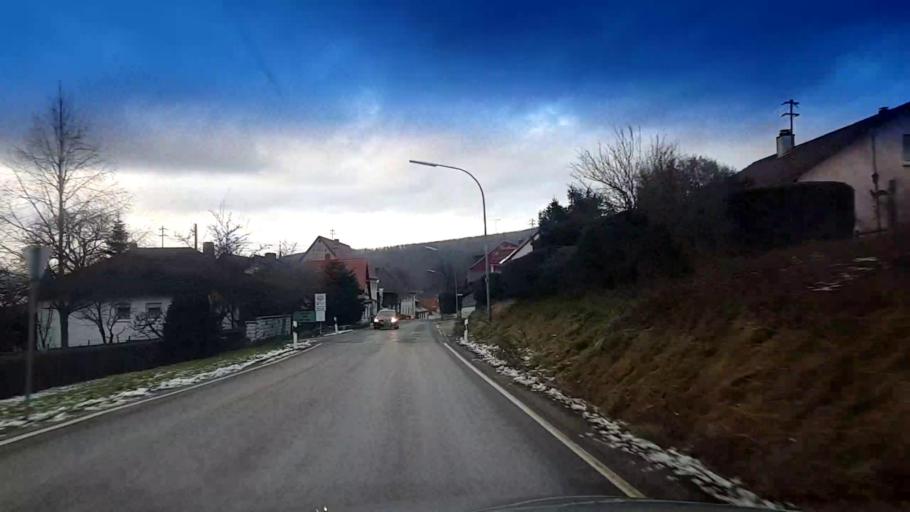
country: DE
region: Bavaria
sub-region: Upper Franconia
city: Litzendorf
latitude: 49.8727
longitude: 11.0696
